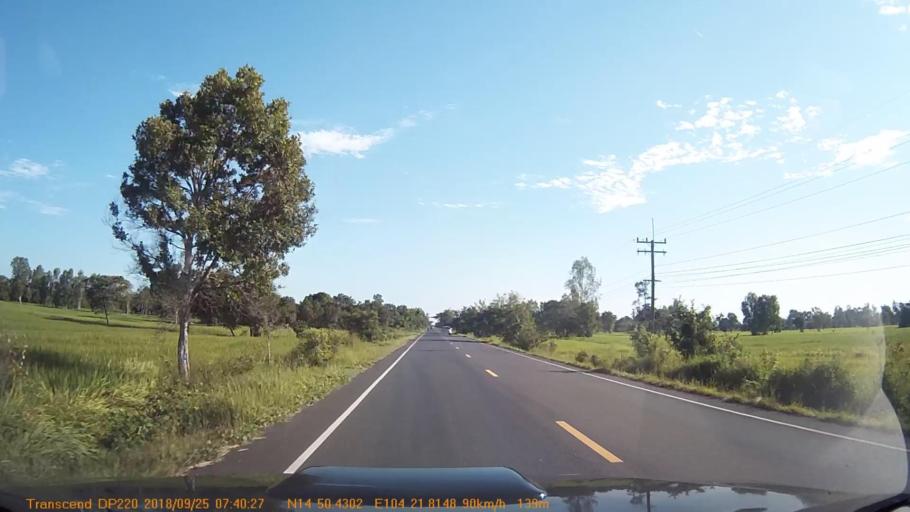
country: TH
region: Sisaket
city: Phayu
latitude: 14.8412
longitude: 104.3638
